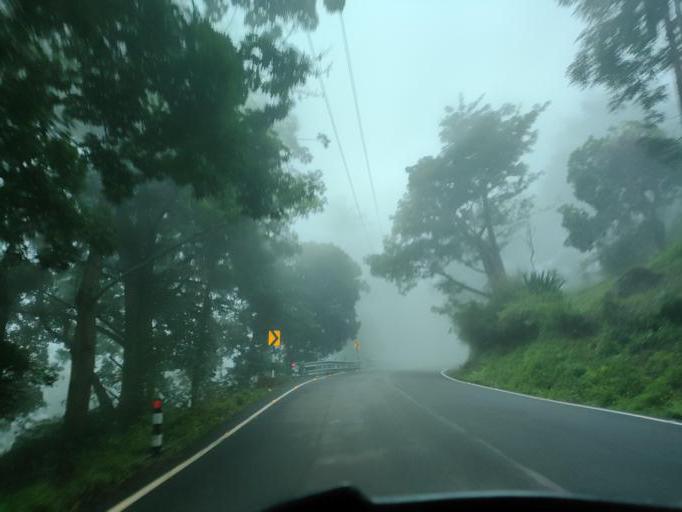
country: IN
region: Tamil Nadu
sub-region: Dindigul
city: Ayakudi
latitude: 10.3542
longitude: 77.5708
